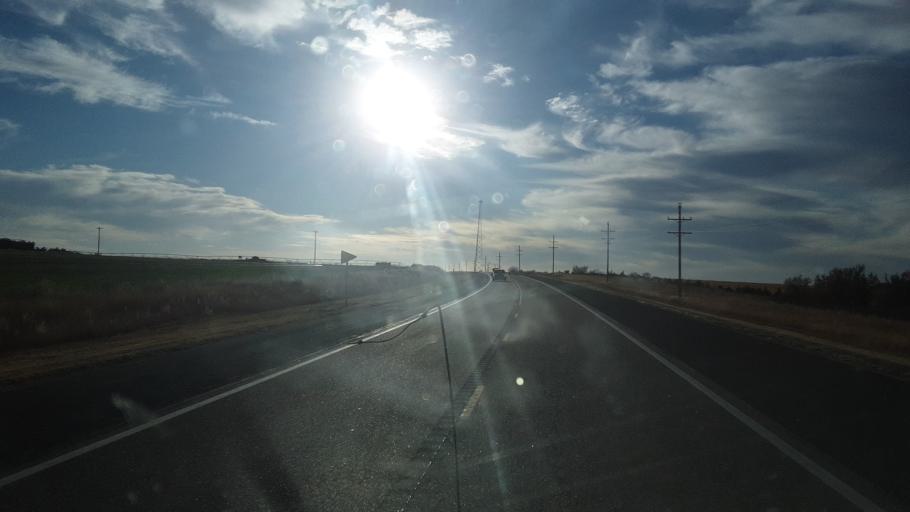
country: US
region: Kansas
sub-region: Kearny County
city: Lakin
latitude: 37.9727
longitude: -101.1924
